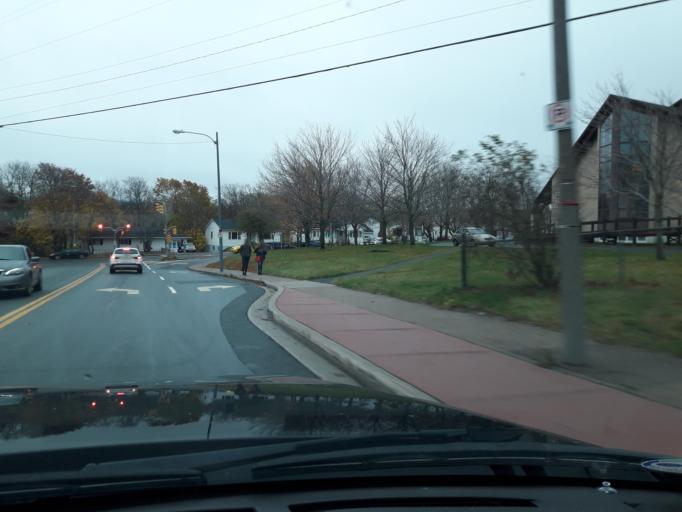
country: CA
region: Newfoundland and Labrador
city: St. John's
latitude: 47.5693
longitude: -52.7348
